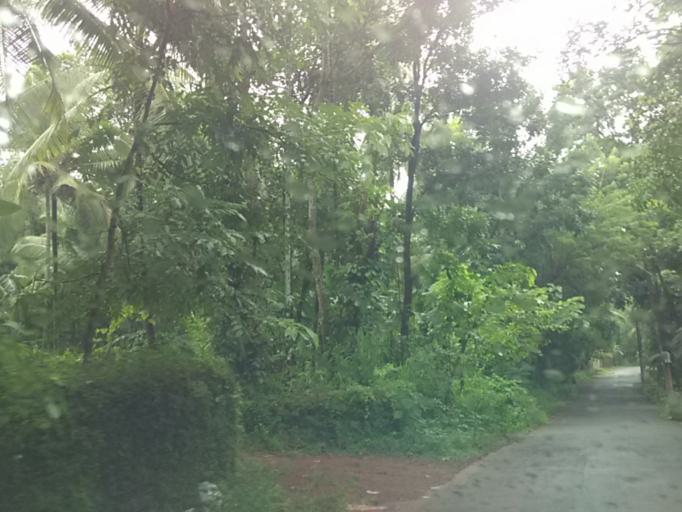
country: IN
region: Kerala
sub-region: Kozhikode
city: Kunnamangalam
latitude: 11.2910
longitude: 75.8883
